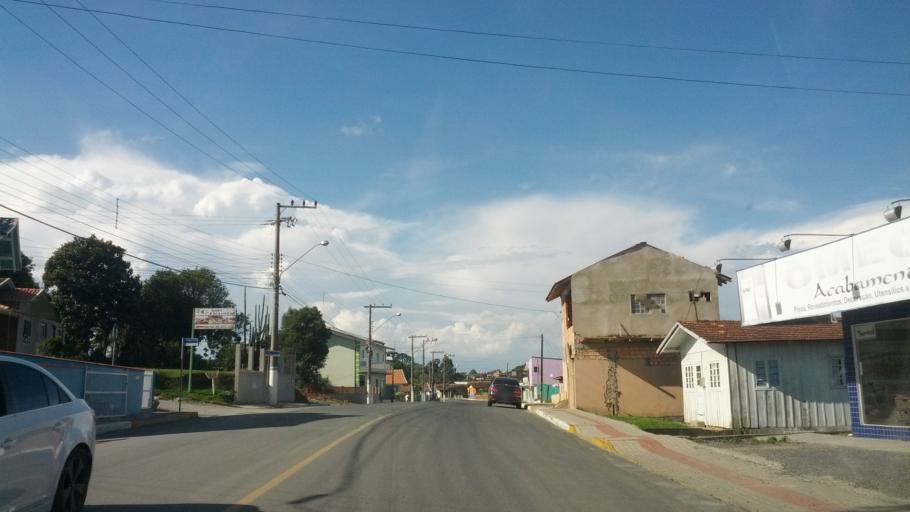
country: BR
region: Santa Catarina
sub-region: Otacilio Costa
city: Otacilio Costa
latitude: -27.4918
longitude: -50.1229
